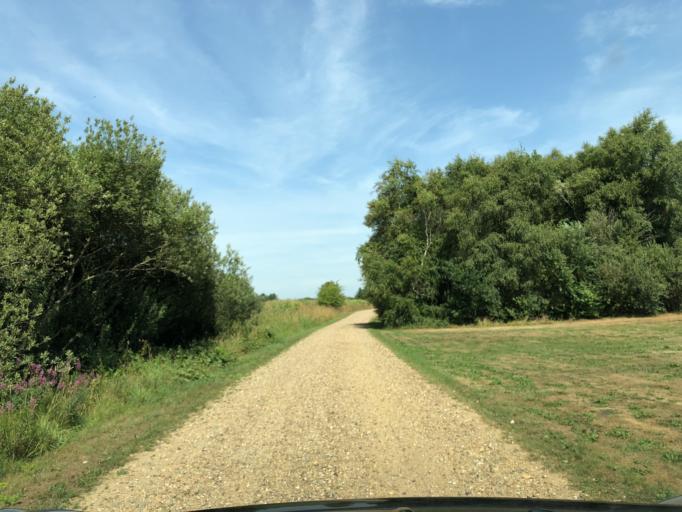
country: DK
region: Central Jutland
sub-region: Ringkobing-Skjern Kommune
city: Skjern
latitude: 55.9916
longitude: 8.4935
